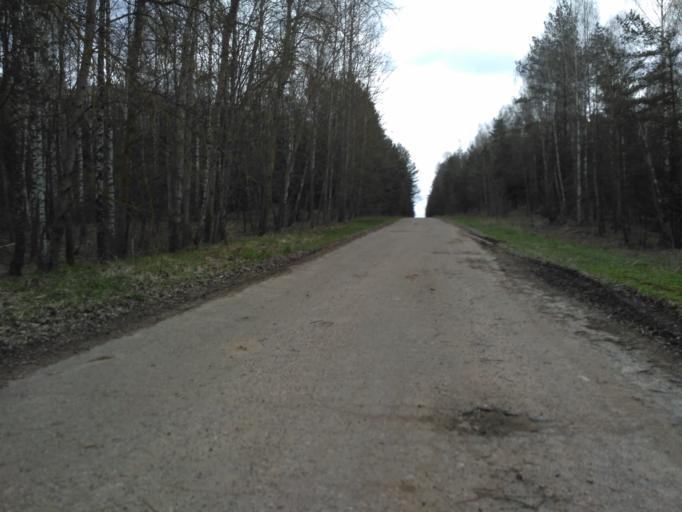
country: BY
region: Minsk
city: Slabada
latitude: 54.0316
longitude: 27.8993
